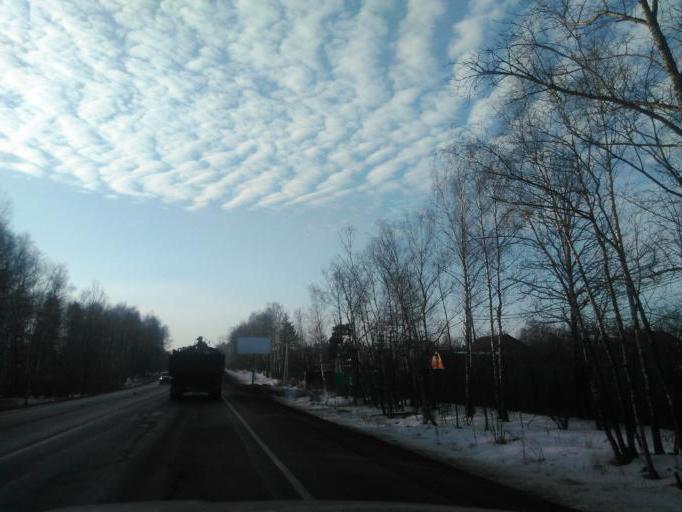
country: RU
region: Moskovskaya
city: Snegiri
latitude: 55.8828
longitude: 36.9438
